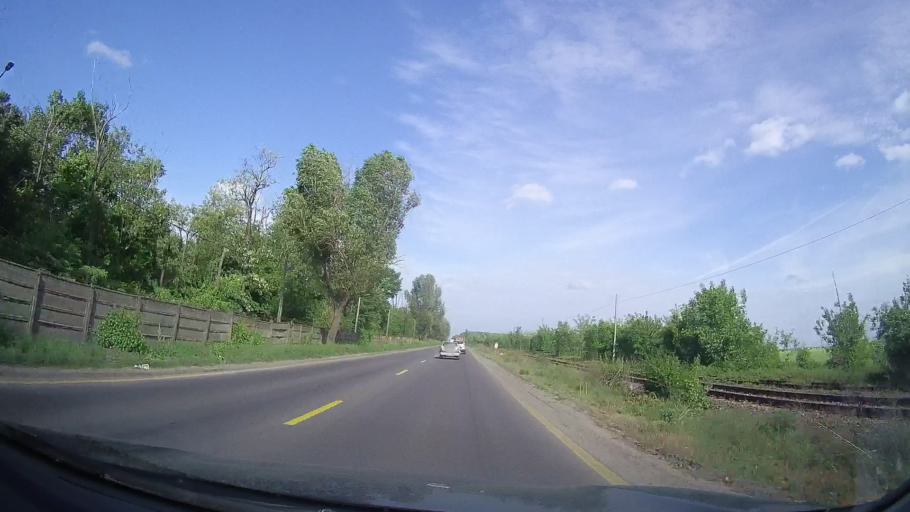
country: RO
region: Ilfov
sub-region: Comuna Magurele
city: Alunisu
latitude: 44.3484
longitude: 26.0696
